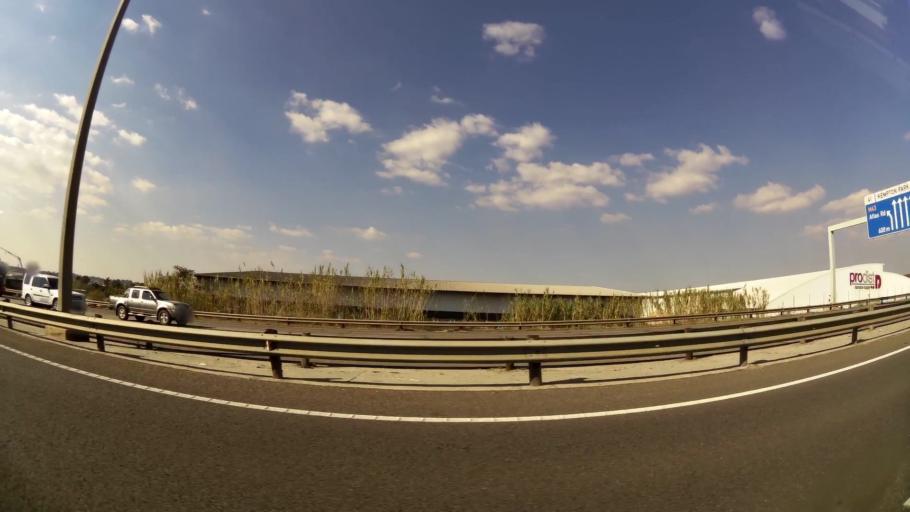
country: ZA
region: Gauteng
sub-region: City of Johannesburg Metropolitan Municipality
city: Modderfontein
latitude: -26.0962
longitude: 28.2634
